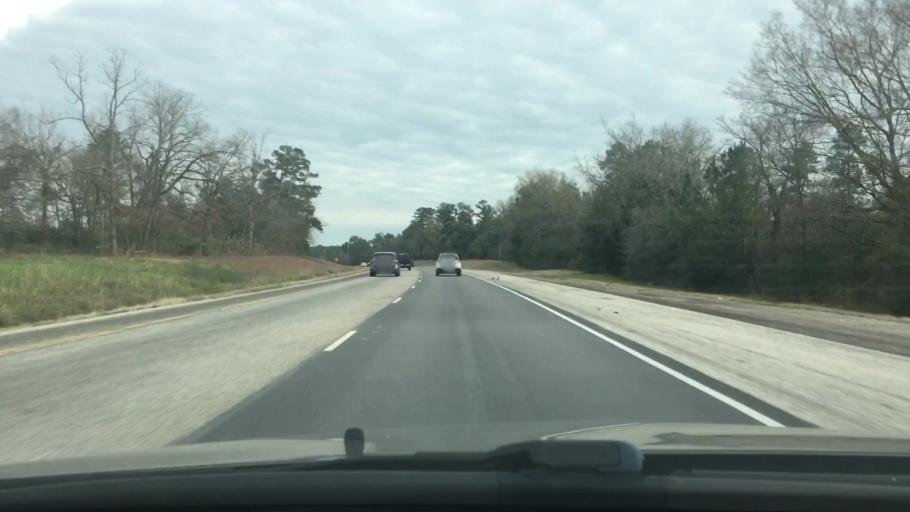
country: US
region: Texas
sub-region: Walker County
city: Huntsville
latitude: 30.7965
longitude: -95.6801
